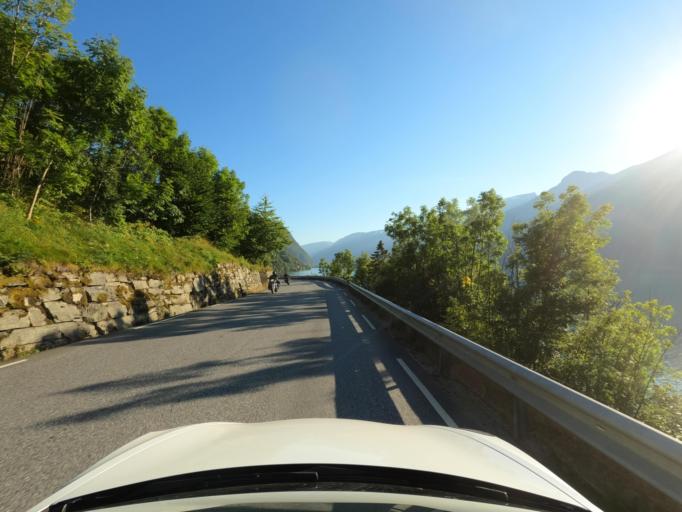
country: NO
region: Hordaland
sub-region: Odda
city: Odda
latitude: 60.2119
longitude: 6.6024
